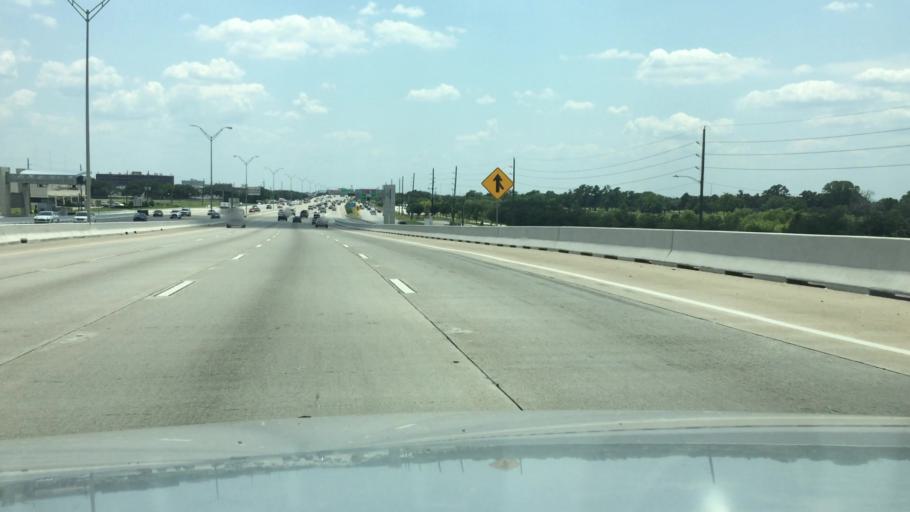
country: US
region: Texas
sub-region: Fort Bend County
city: Meadows Place
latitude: 29.7027
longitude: -95.5574
